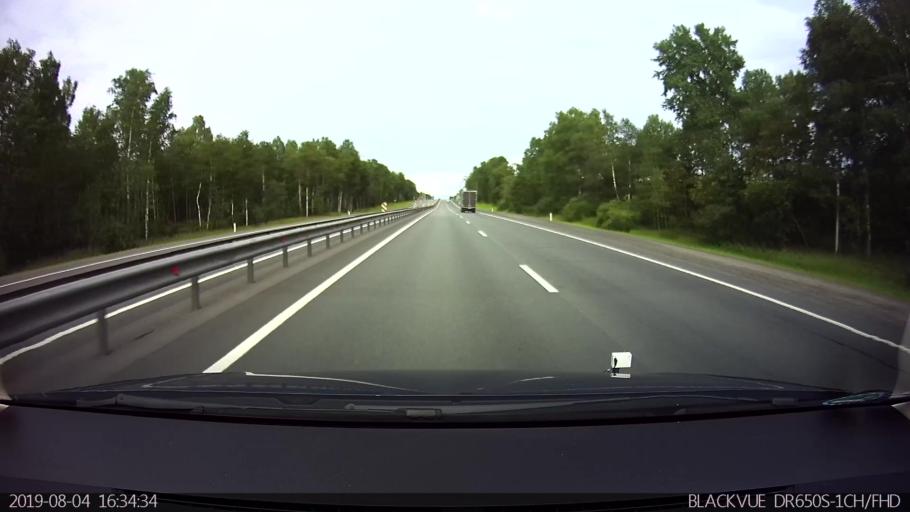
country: RU
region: Smolensk
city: Kholm-Zhirkovskiy
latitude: 55.1877
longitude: 33.7455
